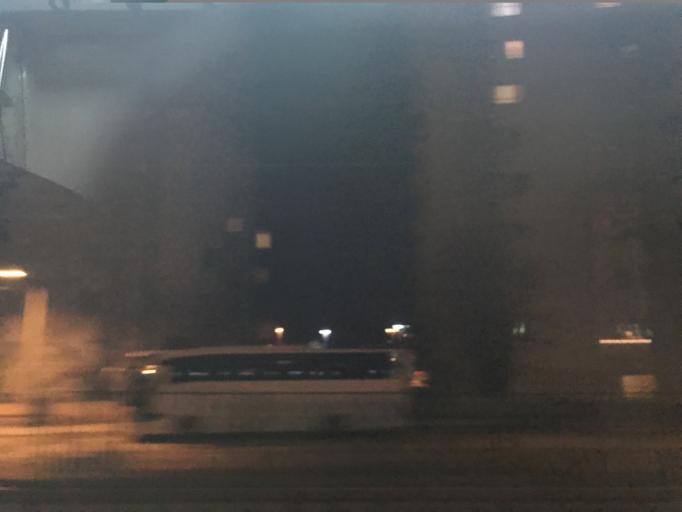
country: TR
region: Istanbul
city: Adalar
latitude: 40.8881
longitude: 29.1790
